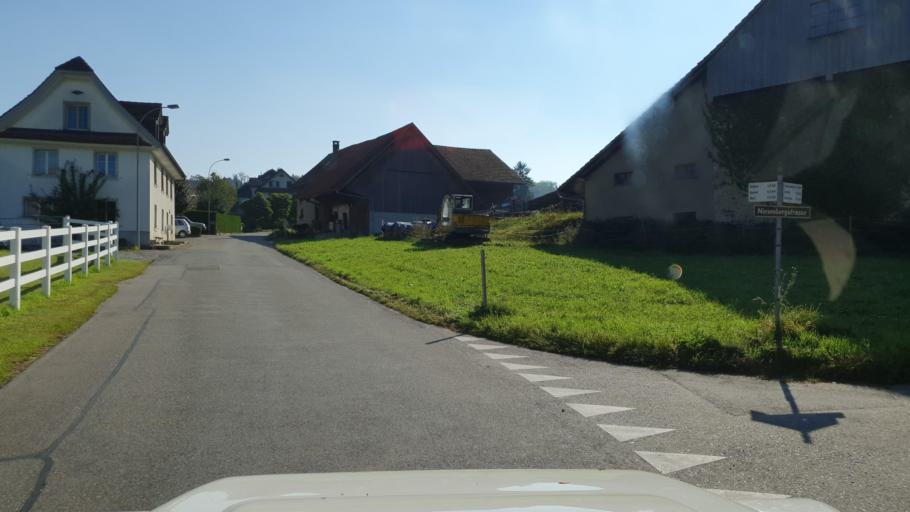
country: CH
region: Aargau
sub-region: Bezirk Bremgarten
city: Sarmenstorf
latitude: 47.3156
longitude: 8.2760
